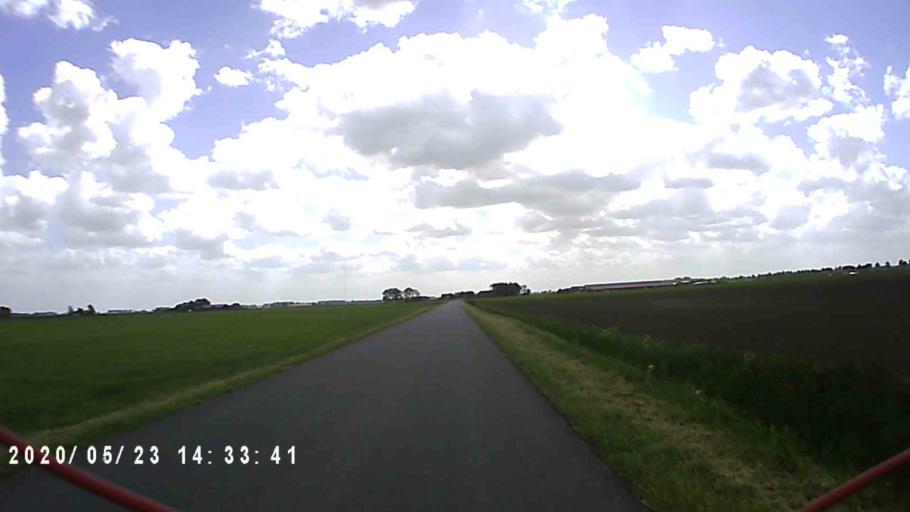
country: NL
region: Groningen
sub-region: Gemeente Delfzijl
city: Delfzijl
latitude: 53.2788
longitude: 6.9649
